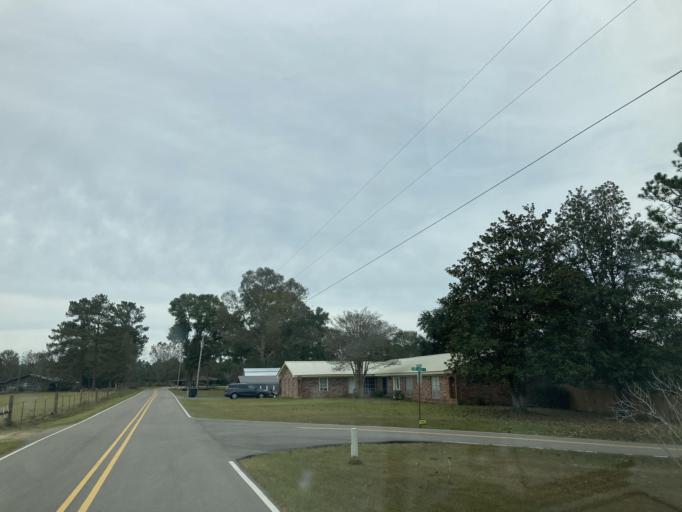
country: US
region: Mississippi
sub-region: Lamar County
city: Purvis
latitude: 31.1102
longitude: -89.4184
